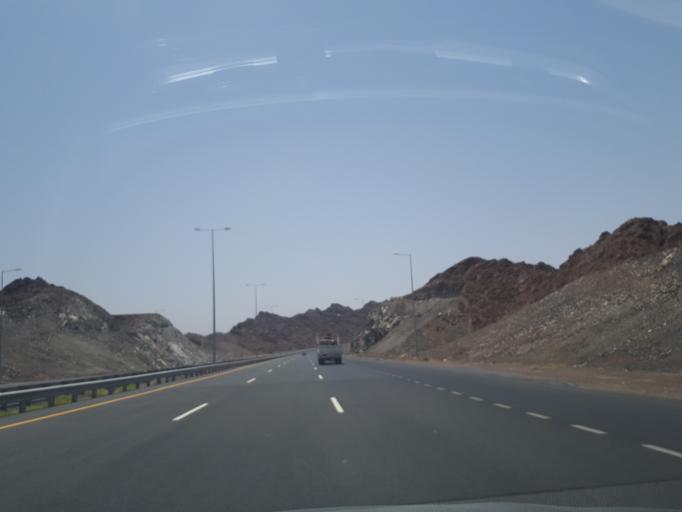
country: OM
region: Ash Sharqiyah
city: Ibra'
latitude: 22.7191
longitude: 58.5756
